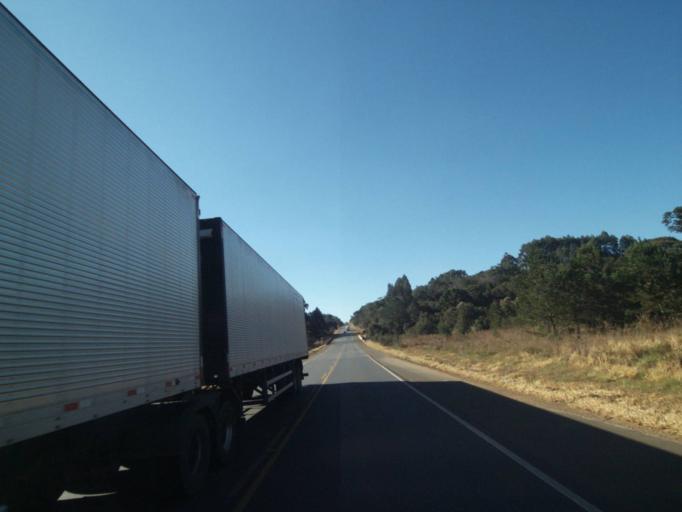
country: BR
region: Parana
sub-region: Tibagi
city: Tibagi
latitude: -24.6119
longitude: -50.4446
